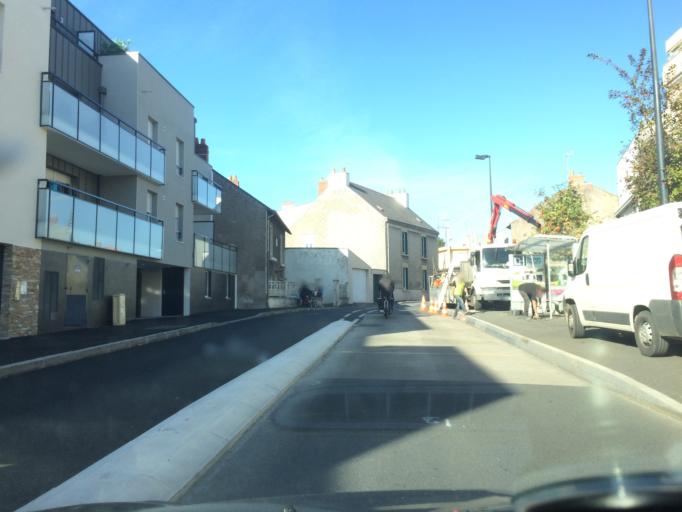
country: FR
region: Pays de la Loire
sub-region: Departement de la Loire-Atlantique
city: Nantes
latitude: 47.2356
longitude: -1.5411
